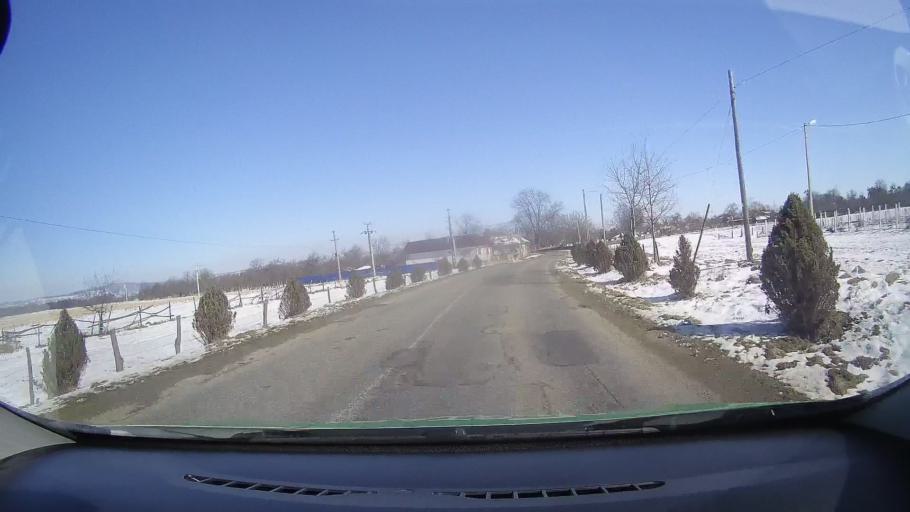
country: RO
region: Brasov
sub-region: Oras Victoria
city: Victoria
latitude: 45.7409
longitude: 24.7361
